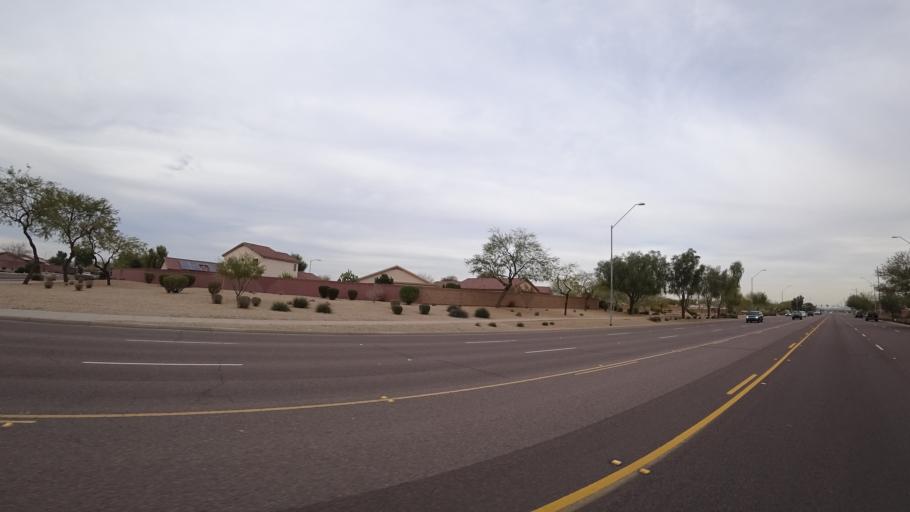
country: US
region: Arizona
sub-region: Maricopa County
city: Surprise
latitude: 33.6093
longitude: -112.3807
